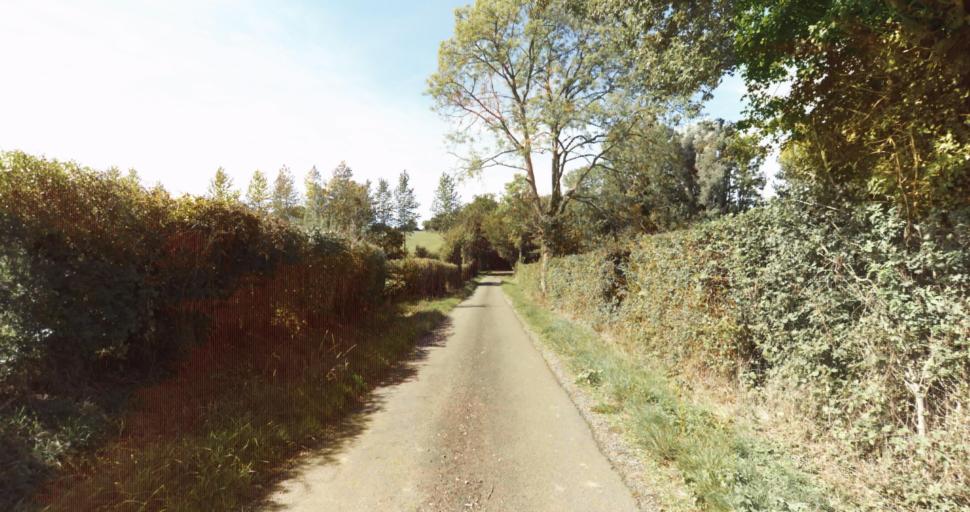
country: FR
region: Lower Normandy
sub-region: Departement de l'Orne
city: Gace
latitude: 48.7514
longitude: 0.2728
